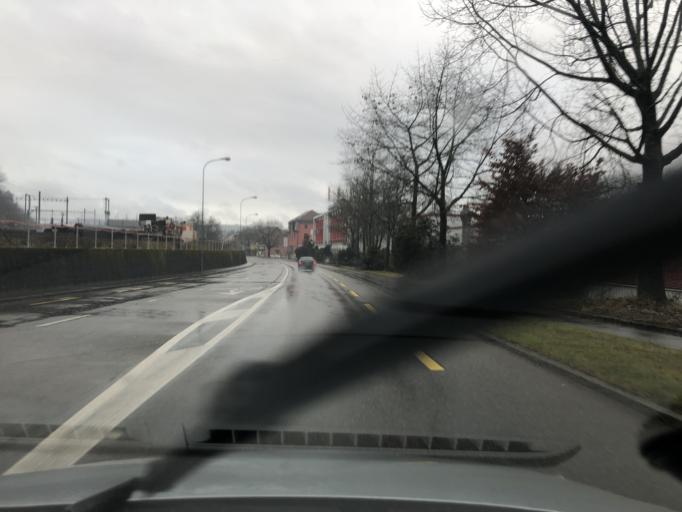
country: CH
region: Aargau
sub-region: Bezirk Zurzach
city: Koblenz
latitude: 47.6025
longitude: 8.2279
